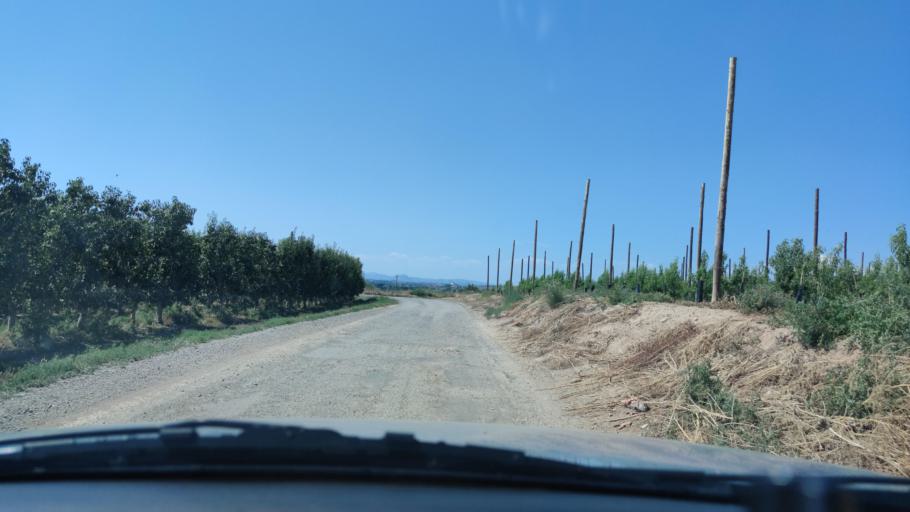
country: ES
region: Catalonia
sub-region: Provincia de Lleida
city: Corbins
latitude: 41.6776
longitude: 0.6701
